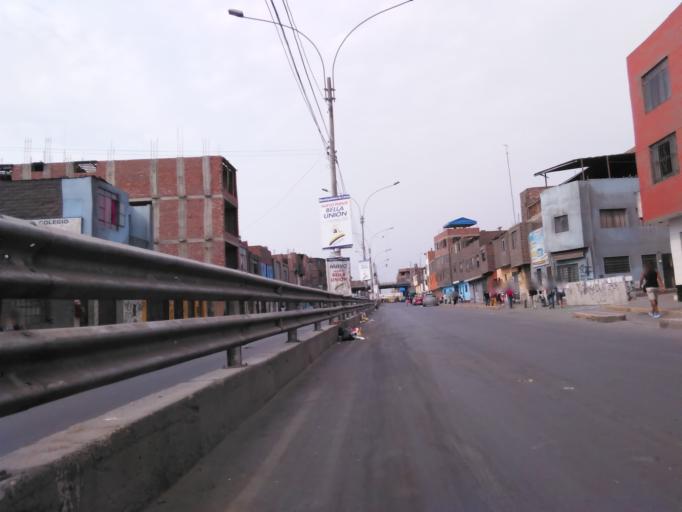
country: PE
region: Callao
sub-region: Callao
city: Callao
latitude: -12.0337
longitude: -77.0782
